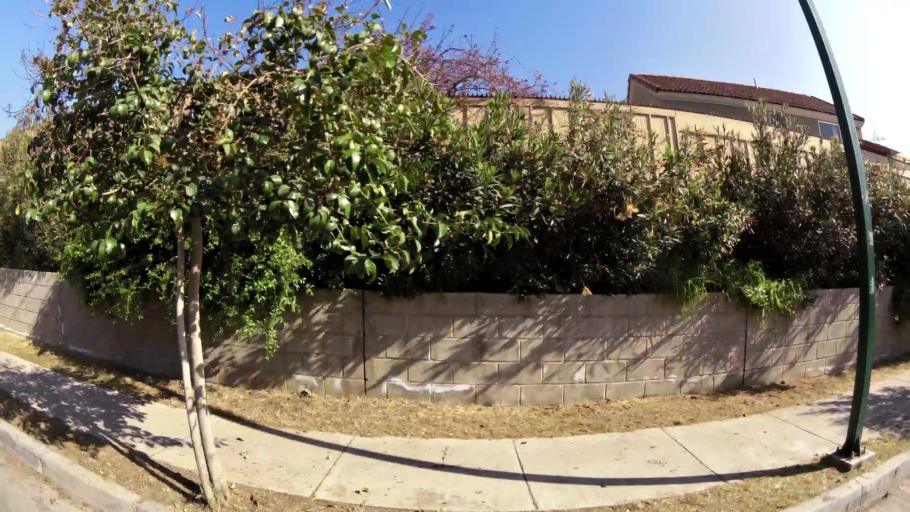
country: CL
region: Santiago Metropolitan
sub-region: Provincia de Chacabuco
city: Chicureo Abajo
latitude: -33.3441
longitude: -70.6760
